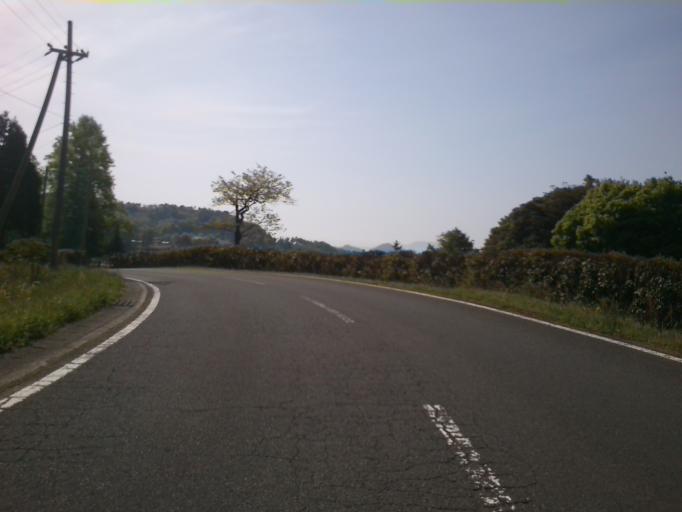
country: JP
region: Kyoto
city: Miyazu
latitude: 35.6278
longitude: 135.2206
